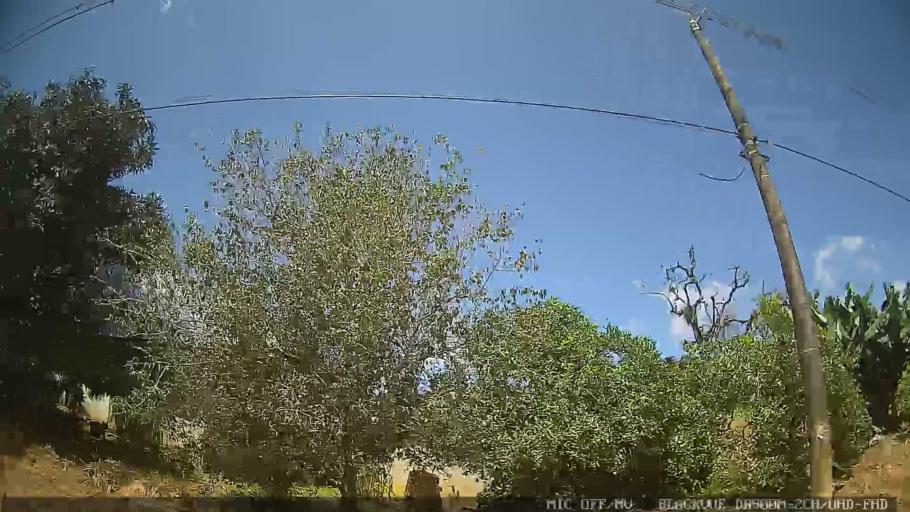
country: BR
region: Sao Paulo
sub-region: Biritiba-Mirim
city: Biritiba Mirim
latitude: -23.5952
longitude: -46.0730
